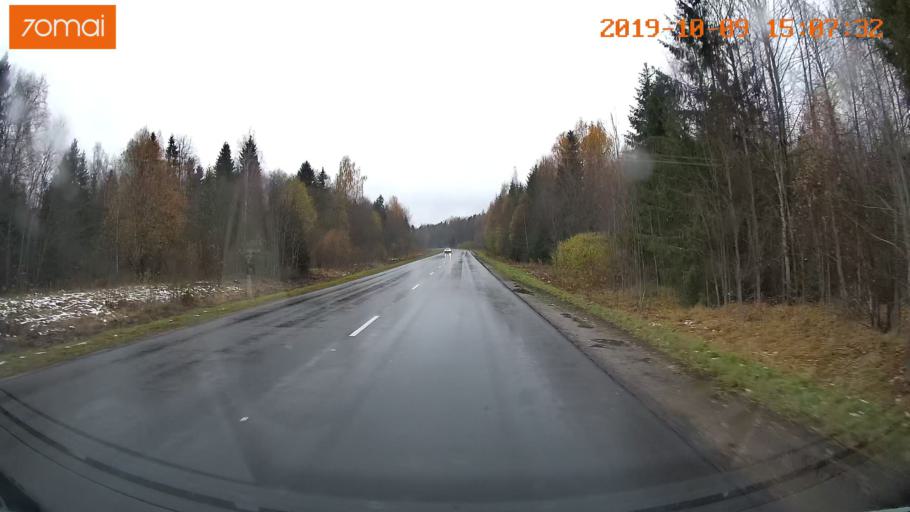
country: RU
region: Kostroma
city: Susanino
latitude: 58.2180
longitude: 41.6492
